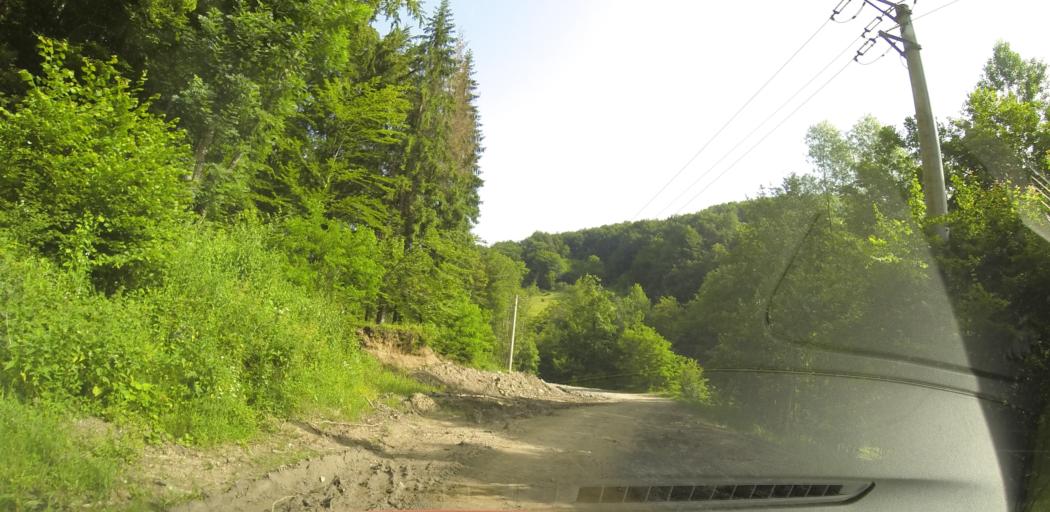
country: RO
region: Valcea
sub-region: Oras Baile Olanesti
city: Baile Olanesti
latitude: 45.2198
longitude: 24.2153
